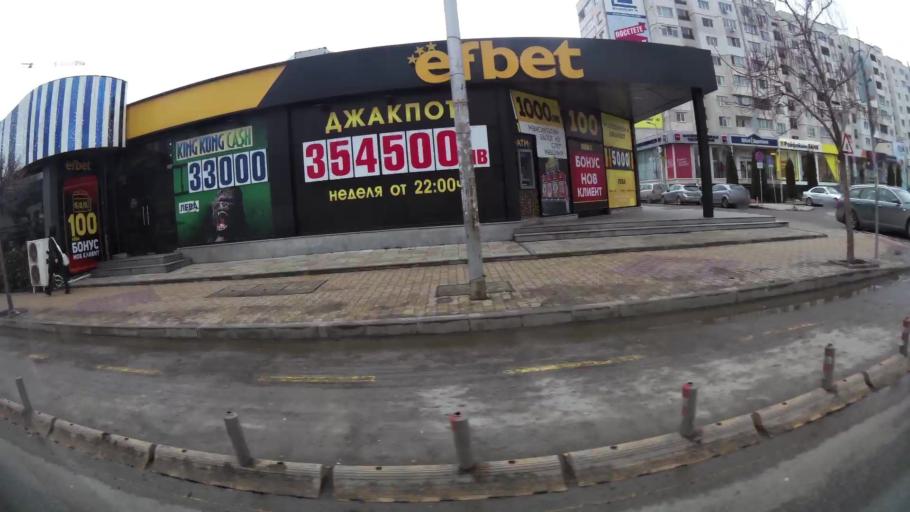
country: BG
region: Sofia-Capital
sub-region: Stolichna Obshtina
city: Sofia
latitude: 42.7259
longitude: 23.3030
